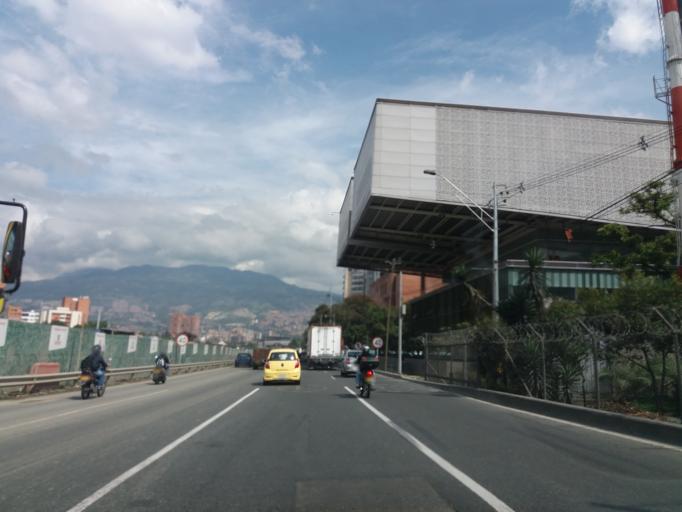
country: CO
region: Antioquia
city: Medellin
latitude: 6.2412
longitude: -75.5773
